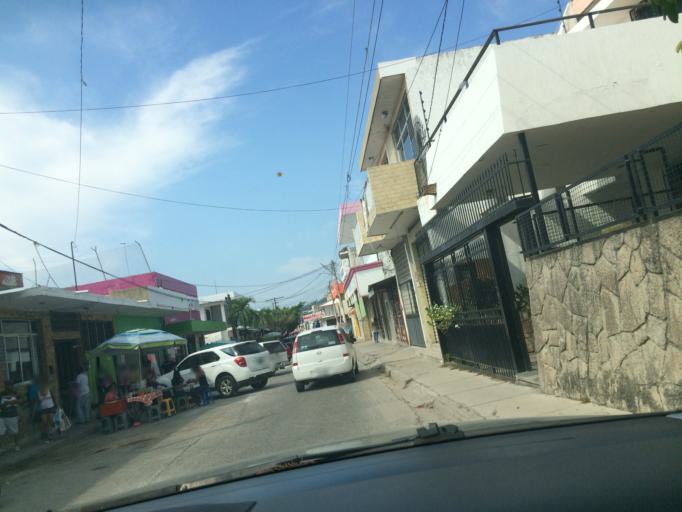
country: MX
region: Jalisco
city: Cihuatlan
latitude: 19.2376
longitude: -104.5597
